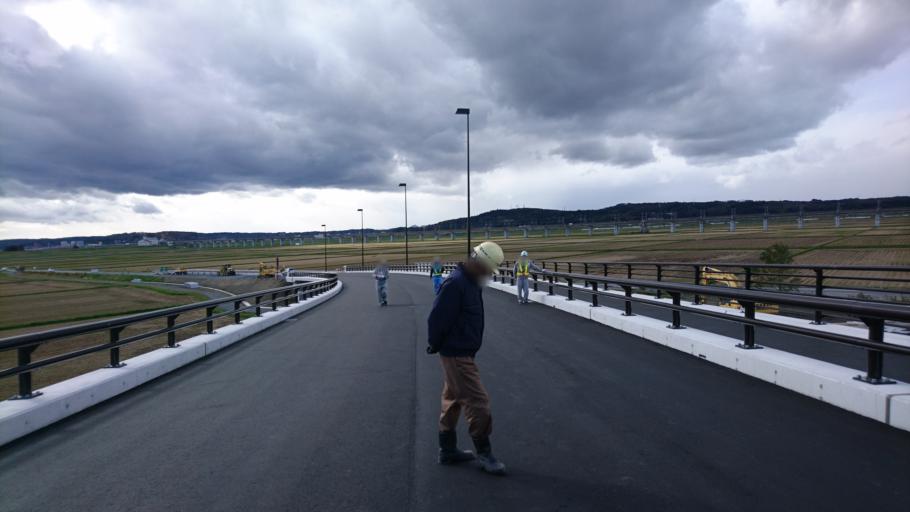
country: JP
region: Iwate
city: Ichinoseki
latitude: 38.9538
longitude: 141.1573
